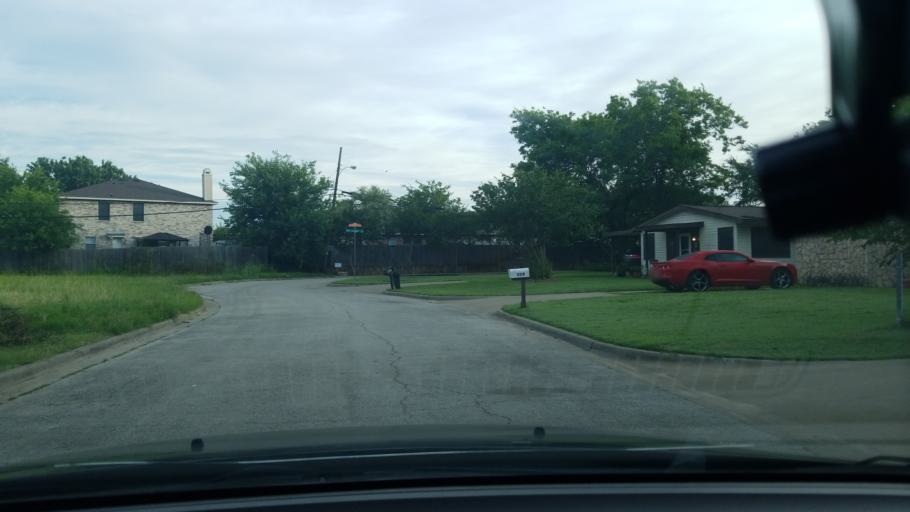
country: US
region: Texas
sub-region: Dallas County
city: Balch Springs
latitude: 32.7640
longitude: -96.6435
